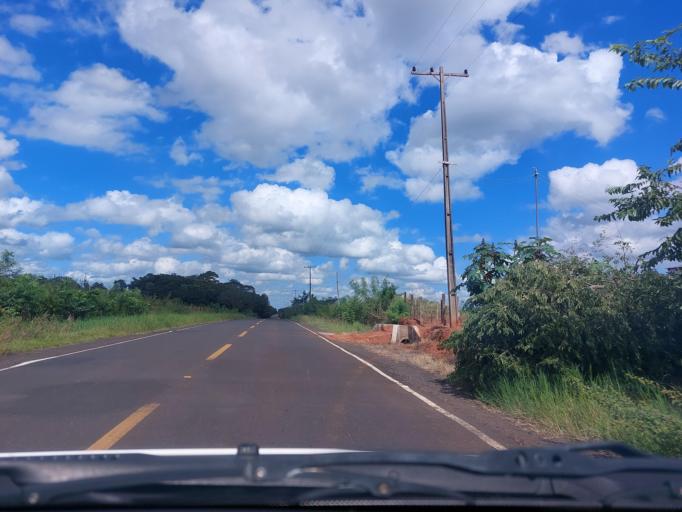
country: PY
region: San Pedro
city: Guayaybi
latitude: -24.5813
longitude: -56.5196
